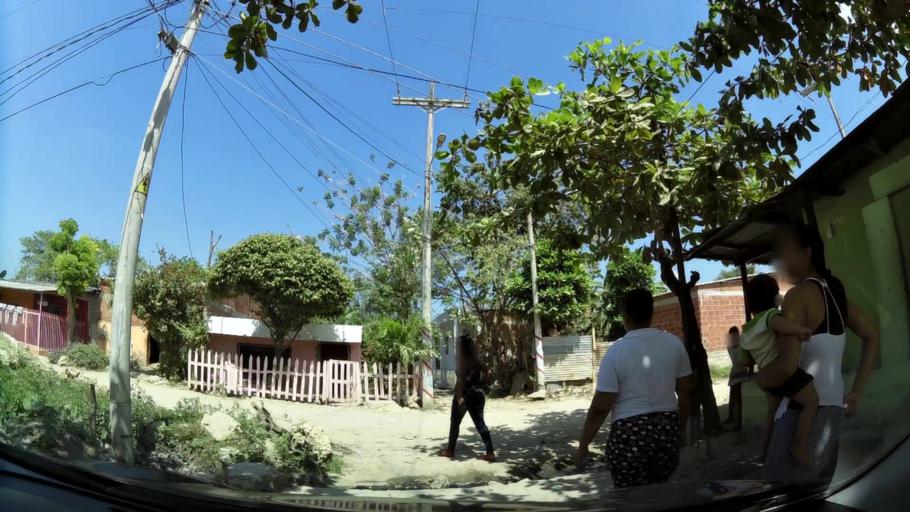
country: CO
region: Bolivar
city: Cartagena
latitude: 10.3463
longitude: -75.4877
